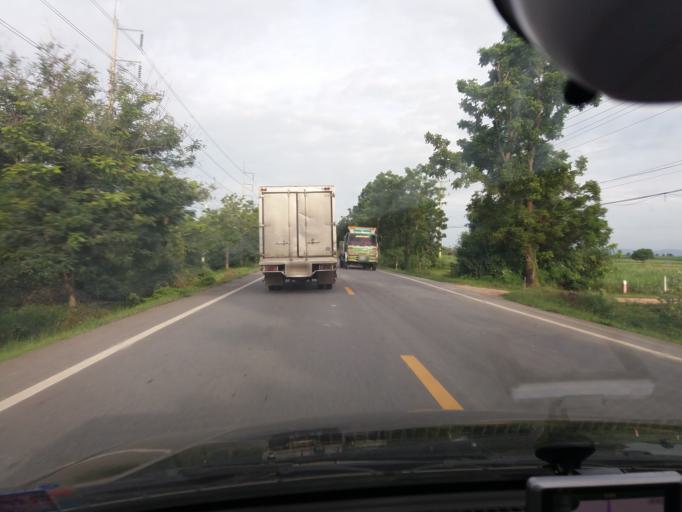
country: TH
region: Kanchanaburi
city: Huai Krachao
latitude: 14.3323
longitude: 99.7367
